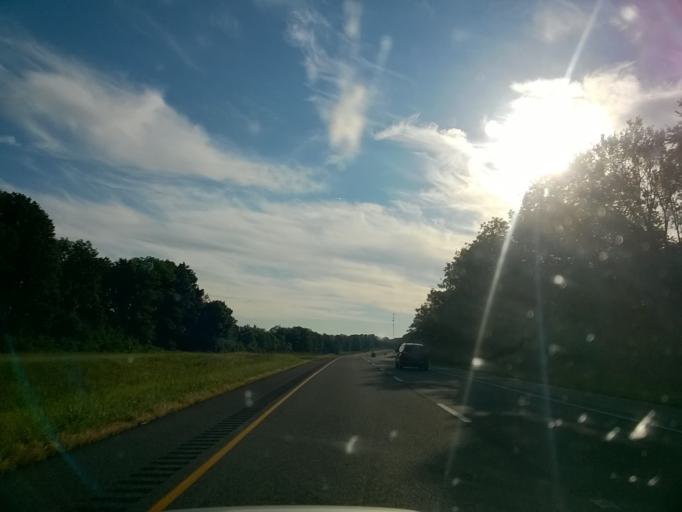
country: US
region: Indiana
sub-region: Warrick County
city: Boonville
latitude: 38.2018
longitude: -87.2137
